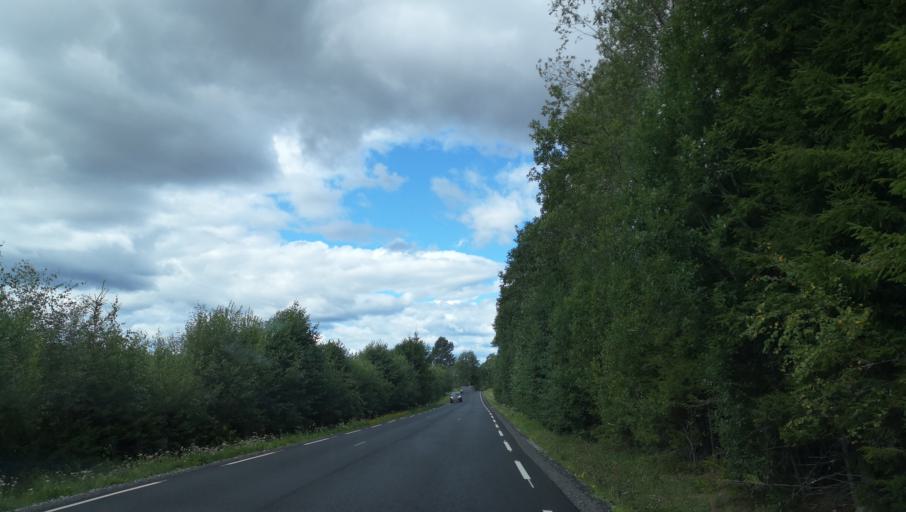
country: NO
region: Ostfold
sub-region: Hobol
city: Elvestad
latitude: 59.6887
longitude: 10.9319
